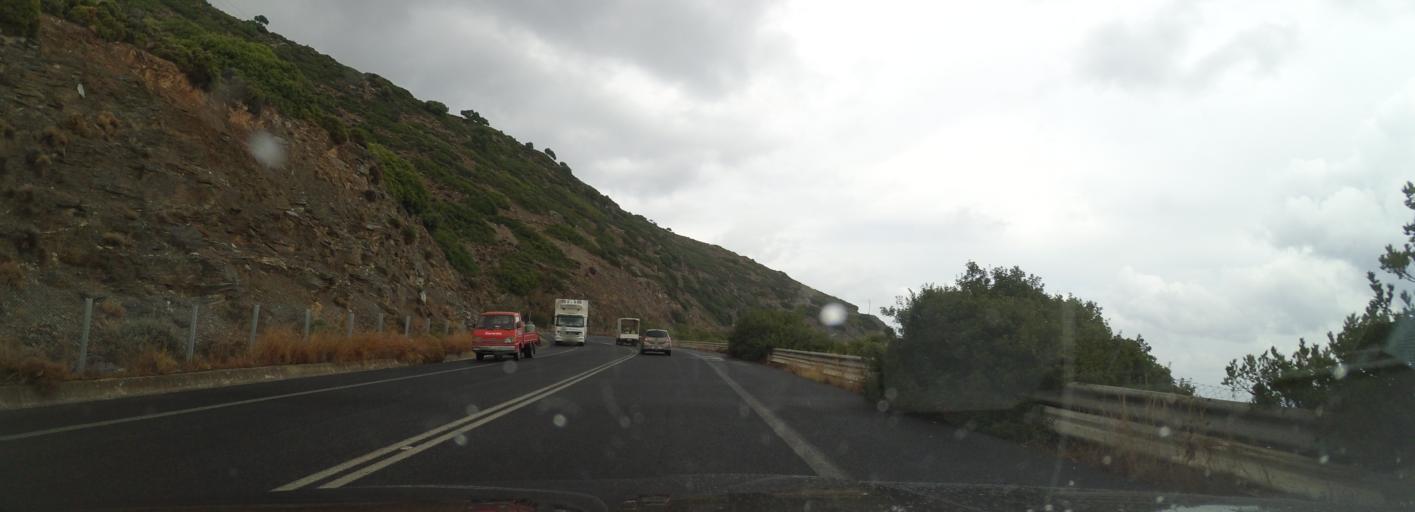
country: GR
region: Crete
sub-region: Nomos Irakleiou
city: Gazi
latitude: 35.3825
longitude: 25.0358
